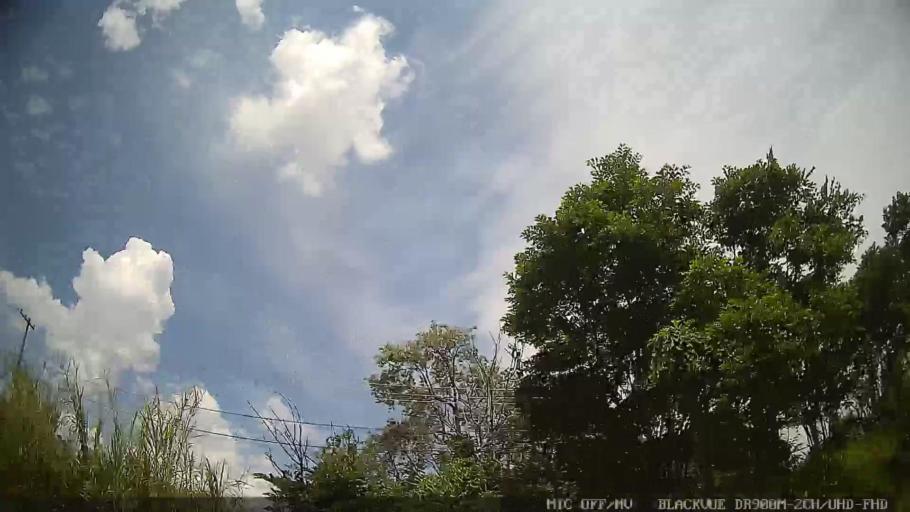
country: BR
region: Sao Paulo
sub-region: Itatiba
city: Itatiba
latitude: -22.9854
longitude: -46.7838
